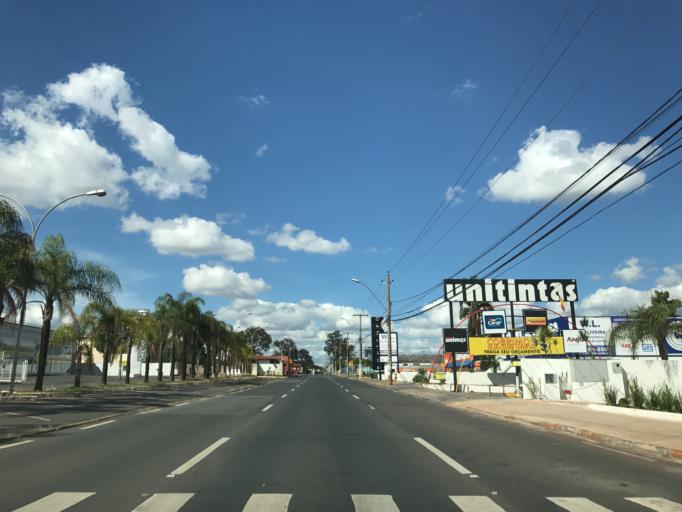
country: BR
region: Federal District
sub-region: Brasilia
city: Brasilia
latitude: -15.8040
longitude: -47.9595
